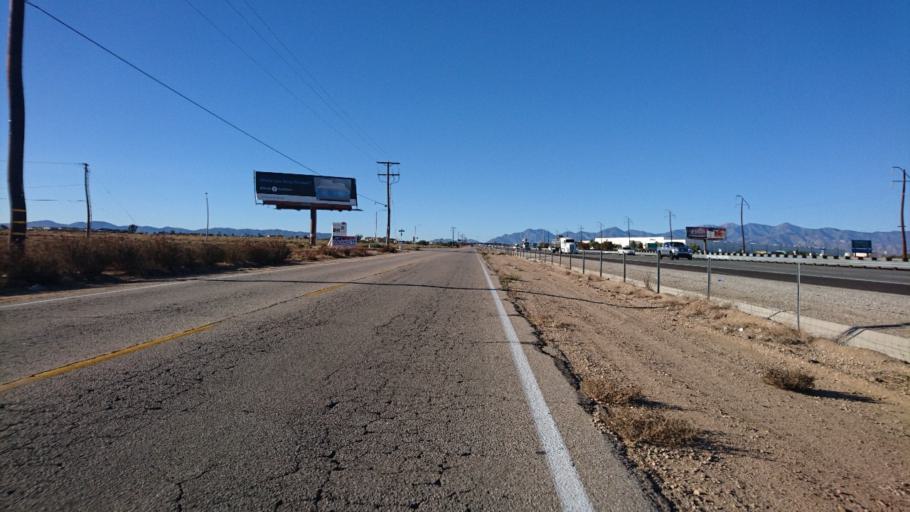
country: US
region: California
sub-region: San Bernardino County
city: Oak Hills
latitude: 34.4387
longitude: -117.3706
